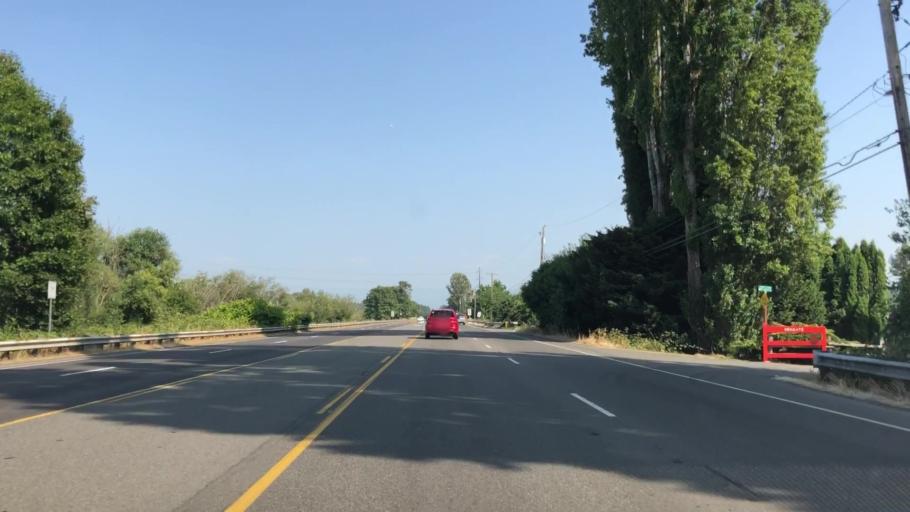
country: US
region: Washington
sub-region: Pierce County
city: Fife
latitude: 47.2289
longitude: -122.3750
